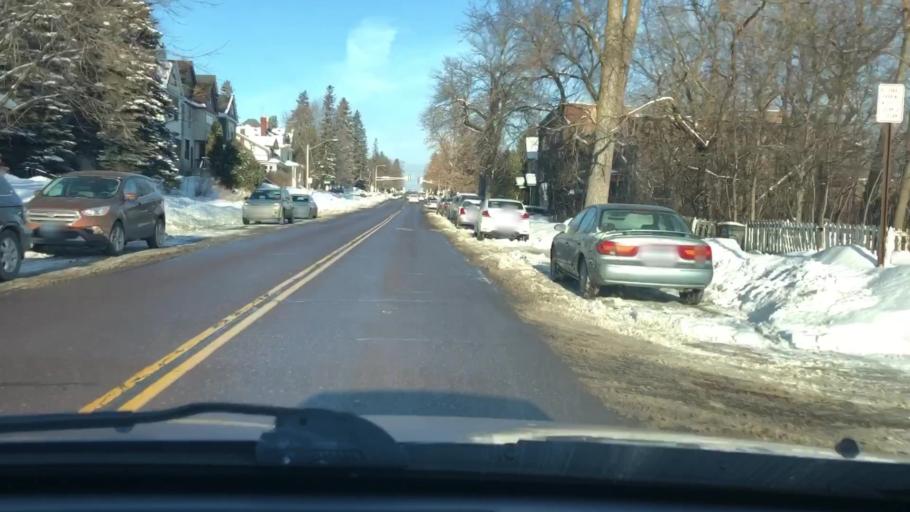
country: US
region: Minnesota
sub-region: Saint Louis County
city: Duluth
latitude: 46.8053
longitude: -92.0742
